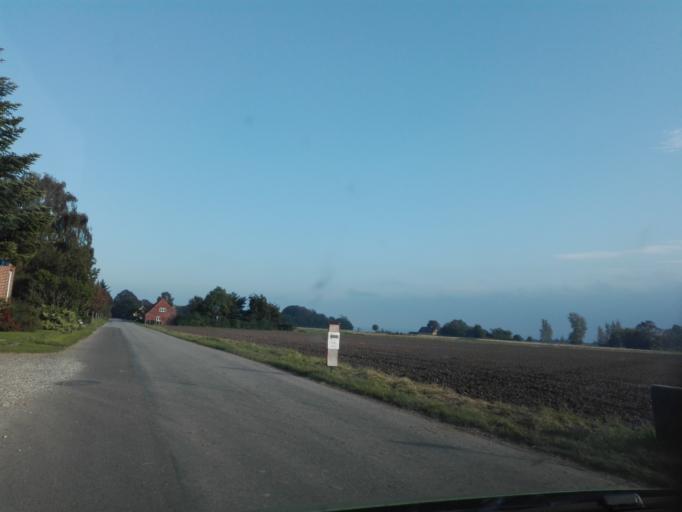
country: DK
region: Central Jutland
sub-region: Odder Kommune
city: Odder
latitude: 55.8909
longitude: 10.1828
